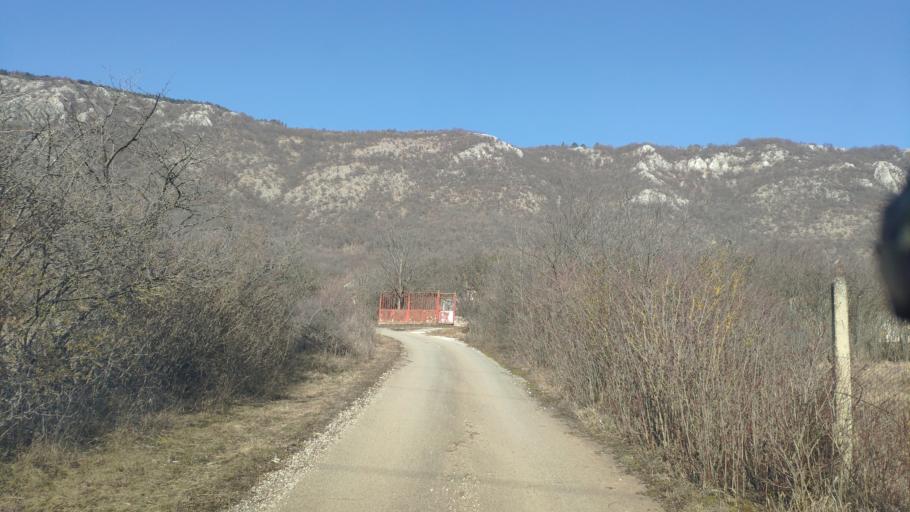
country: SK
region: Kosicky
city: Roznava
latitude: 48.6006
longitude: 20.7214
